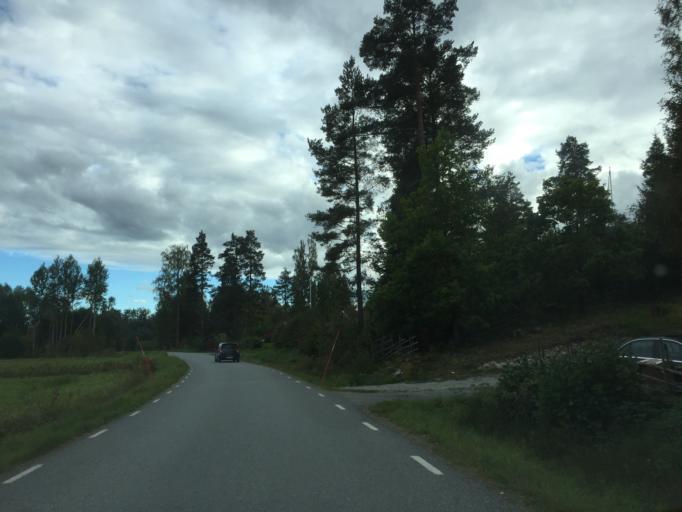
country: SE
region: OErebro
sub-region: Orebro Kommun
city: Hovsta
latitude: 59.3298
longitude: 15.1864
